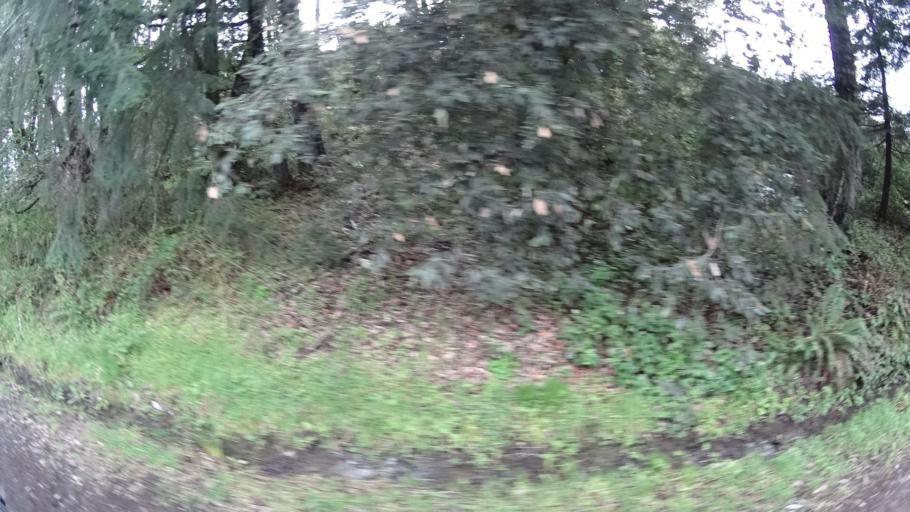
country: US
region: California
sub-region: Humboldt County
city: Blue Lake
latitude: 40.8671
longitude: -123.9063
